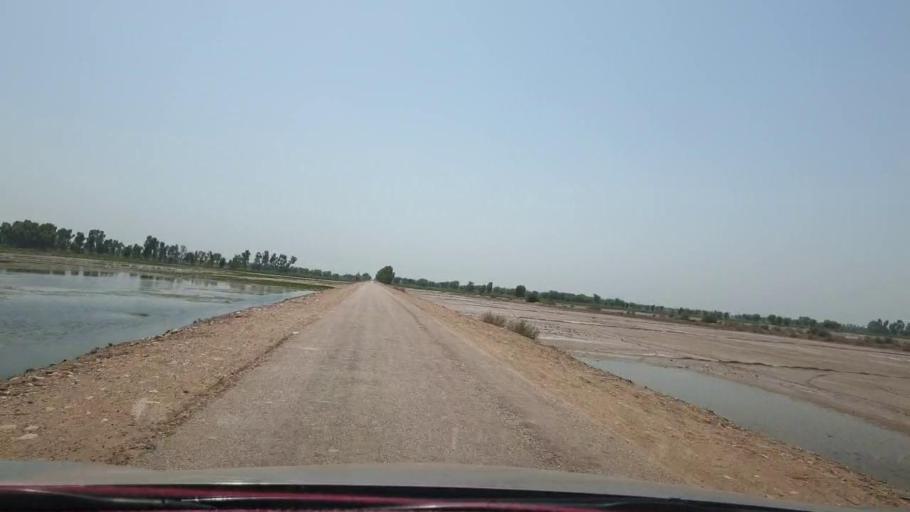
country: PK
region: Sindh
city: Warah
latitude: 27.5442
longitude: 67.7929
